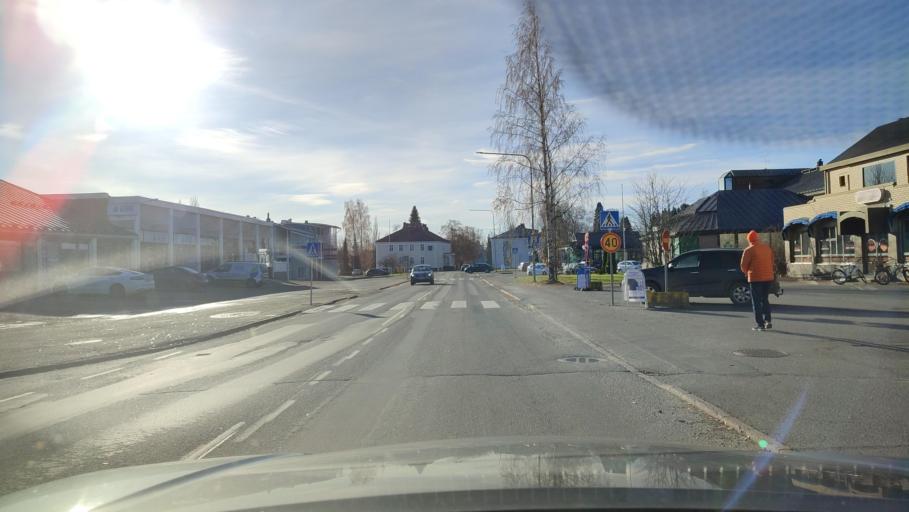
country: FI
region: Southern Ostrobothnia
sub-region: Suupohja
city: Teuva
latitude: 62.4864
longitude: 21.7466
